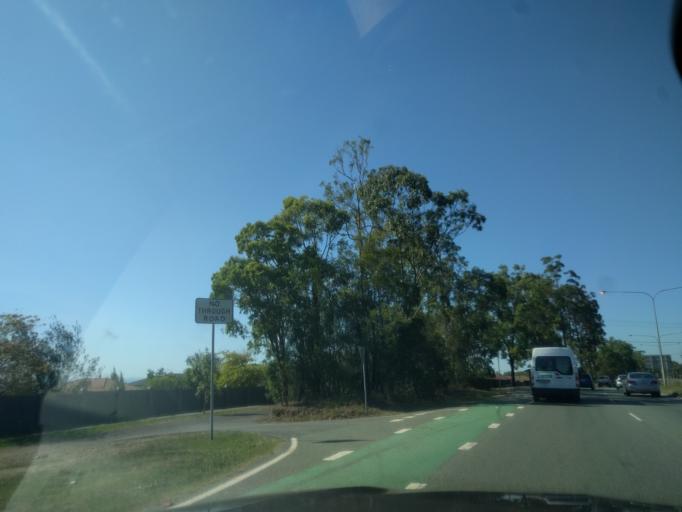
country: AU
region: Queensland
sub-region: Brisbane
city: Sunnybank Hills
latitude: -27.6382
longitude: 153.0447
